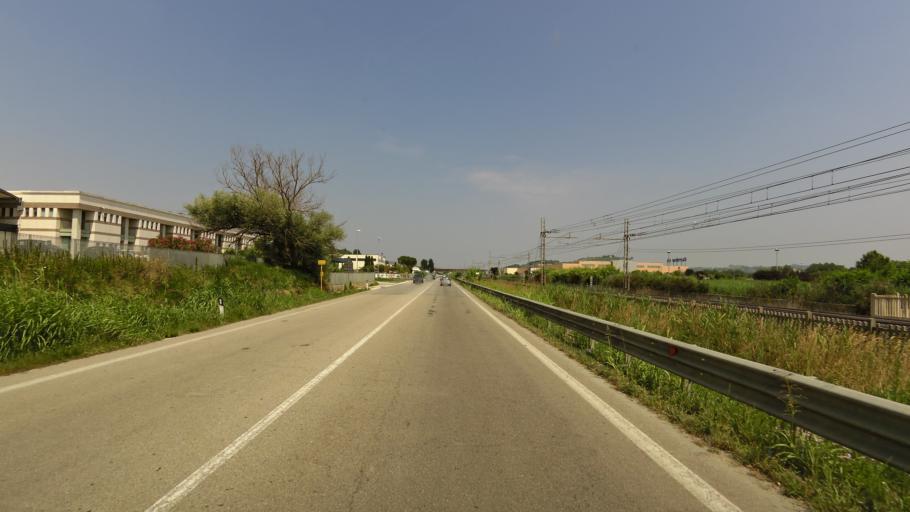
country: IT
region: The Marches
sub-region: Provincia di Ancona
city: Camerano
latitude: 43.5178
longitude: 13.5259
